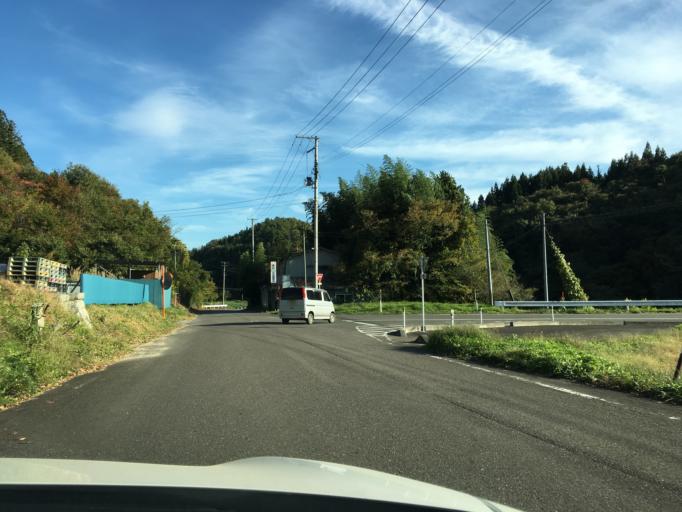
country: JP
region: Fukushima
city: Funehikimachi-funehiki
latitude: 37.2642
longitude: 140.6078
